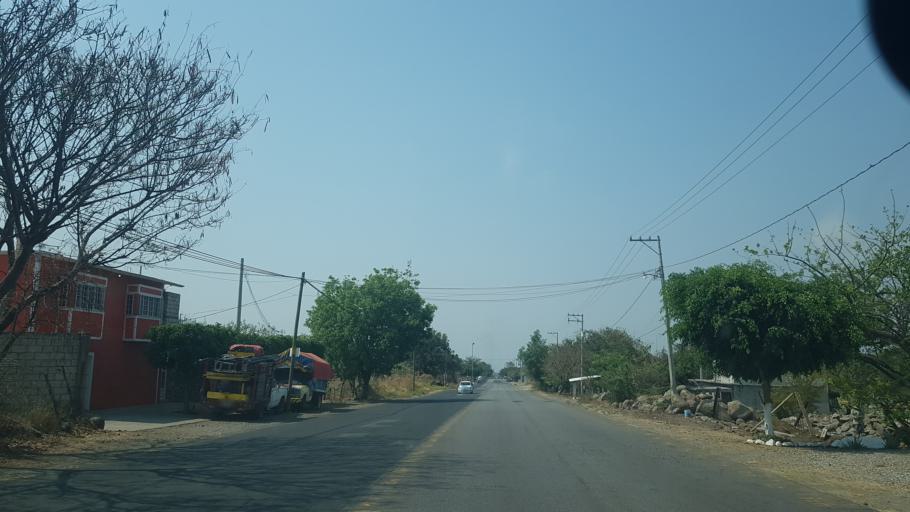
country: MX
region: Morelos
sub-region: Temoac
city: Huazulco
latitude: 18.7493
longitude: -98.7823
